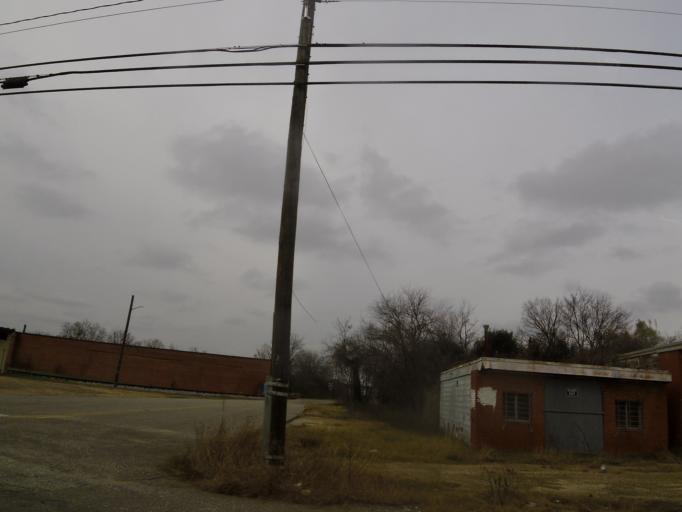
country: US
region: Alabama
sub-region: Montgomery County
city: Montgomery
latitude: 32.3990
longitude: -86.3084
